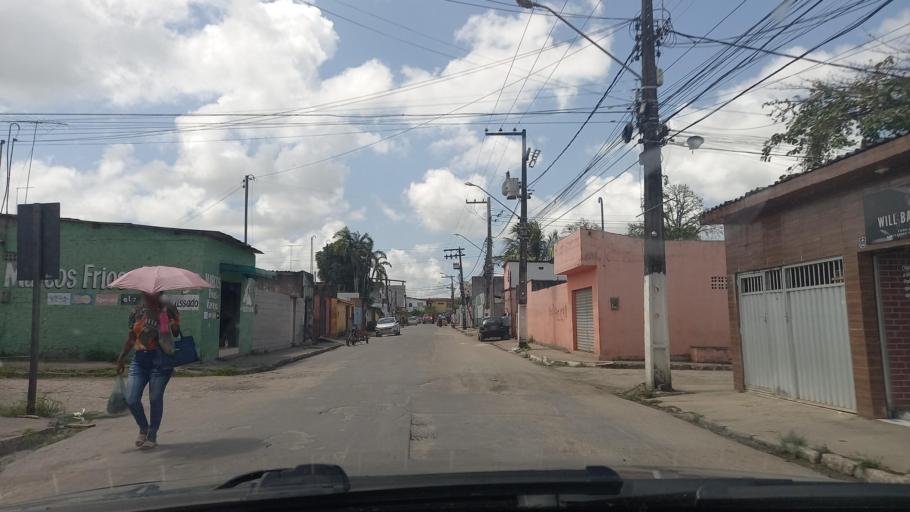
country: BR
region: Pernambuco
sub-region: Goiana
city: Goiana
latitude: -7.5637
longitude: -35.0072
